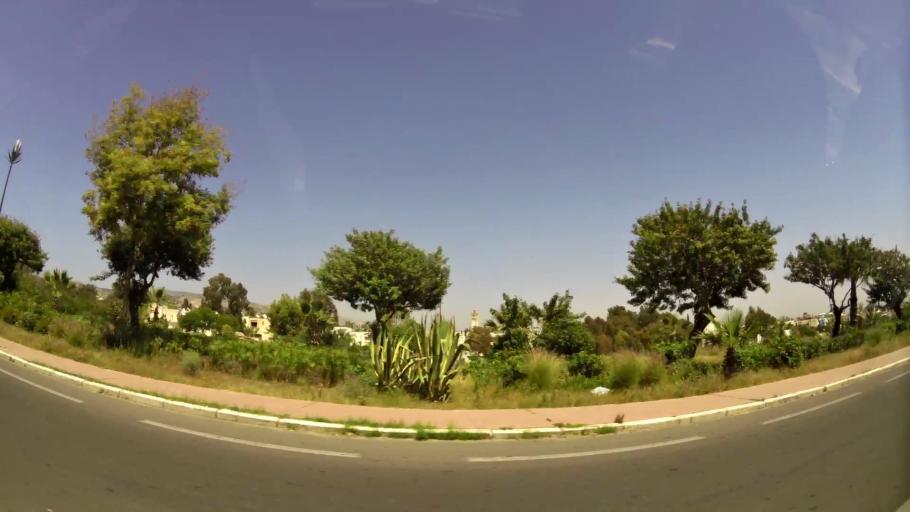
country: MA
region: Souss-Massa-Draa
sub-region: Agadir-Ida-ou-Tnan
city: Agadir
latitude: 30.4327
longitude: -9.5944
